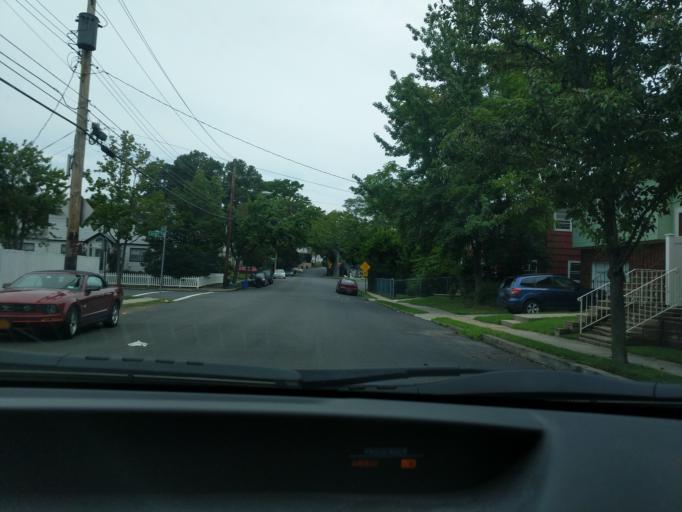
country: US
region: New York
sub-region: Richmond County
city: Staten Island
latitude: 40.5765
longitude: -74.1223
